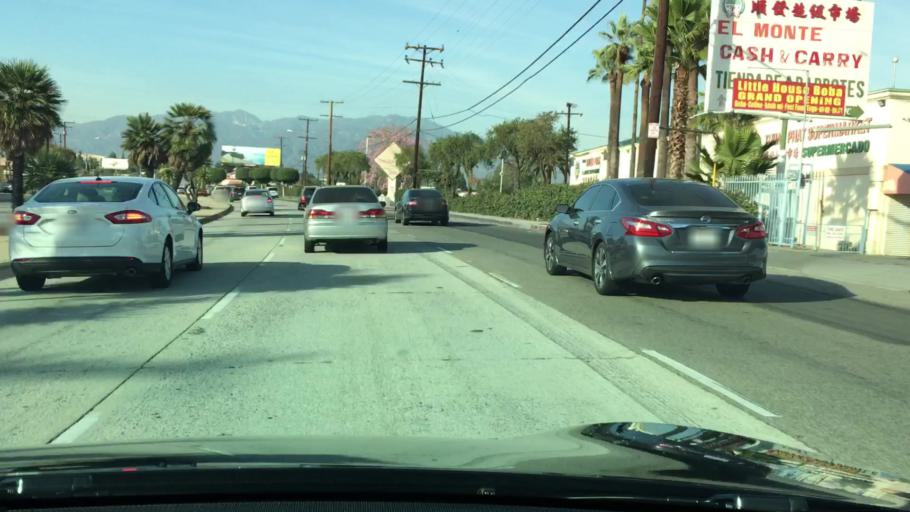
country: US
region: California
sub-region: Los Angeles County
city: South El Monte
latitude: 34.0594
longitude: -118.0643
